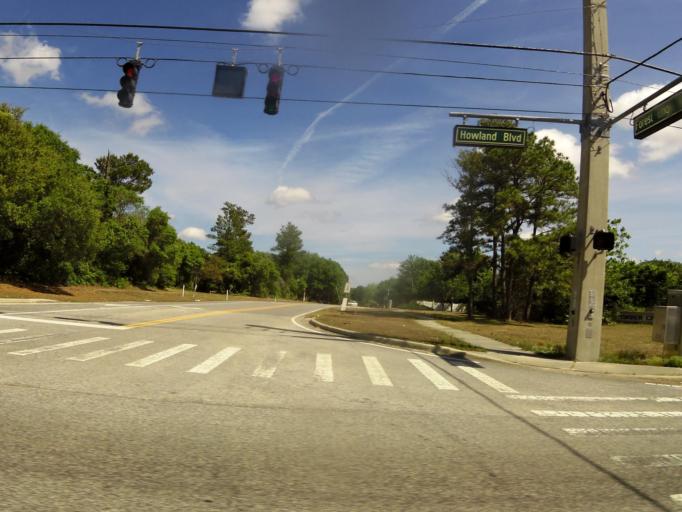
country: US
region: Florida
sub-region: Volusia County
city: Lake Helen
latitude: 28.9486
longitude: -81.2485
